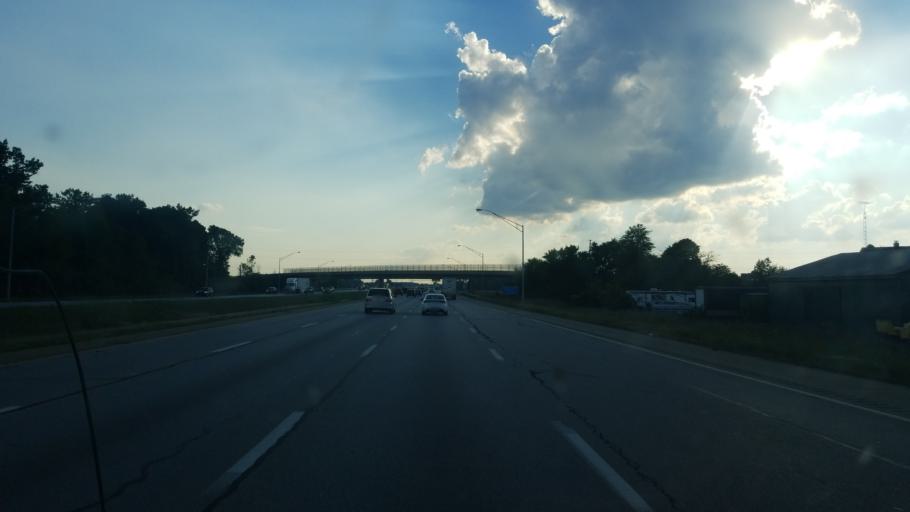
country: US
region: Ohio
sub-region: Wood County
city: Rossford
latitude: 41.5839
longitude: -83.5660
